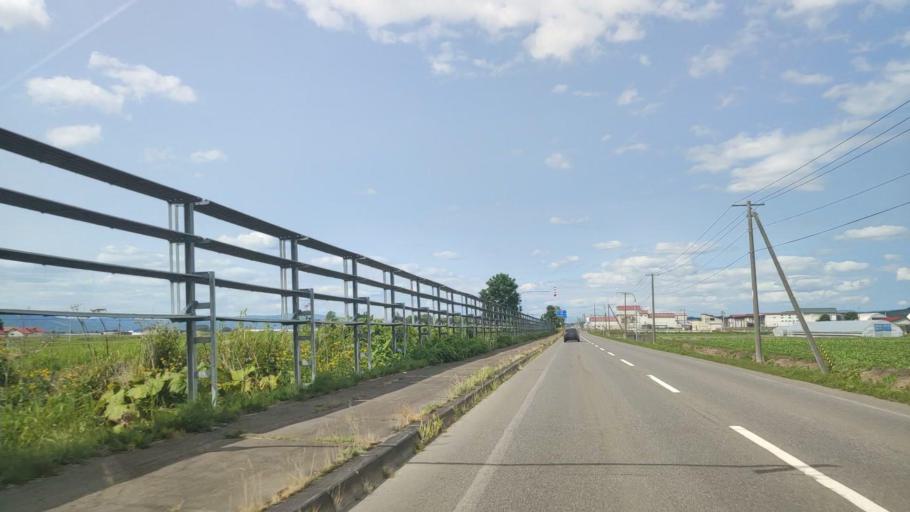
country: JP
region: Hokkaido
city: Nayoro
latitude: 44.1983
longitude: 142.4159
